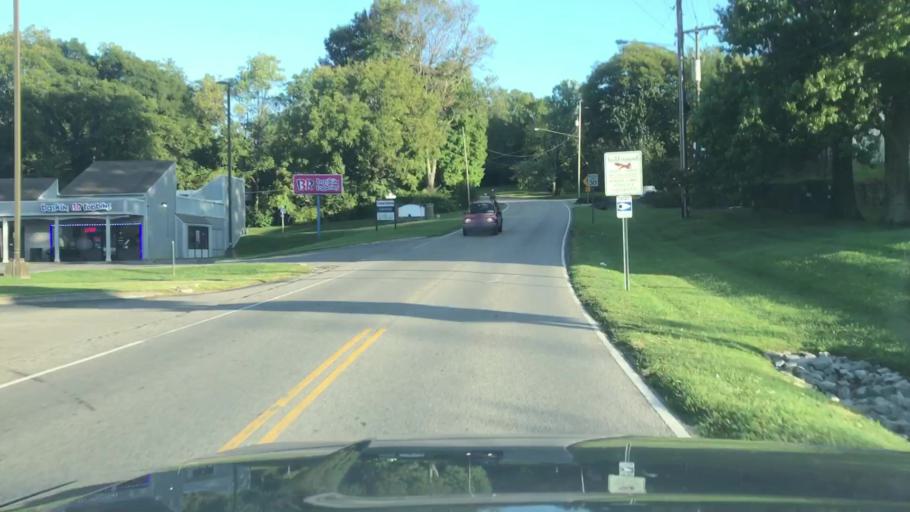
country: US
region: Tennessee
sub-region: Davidson County
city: Belle Meade
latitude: 36.1386
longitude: -86.8800
